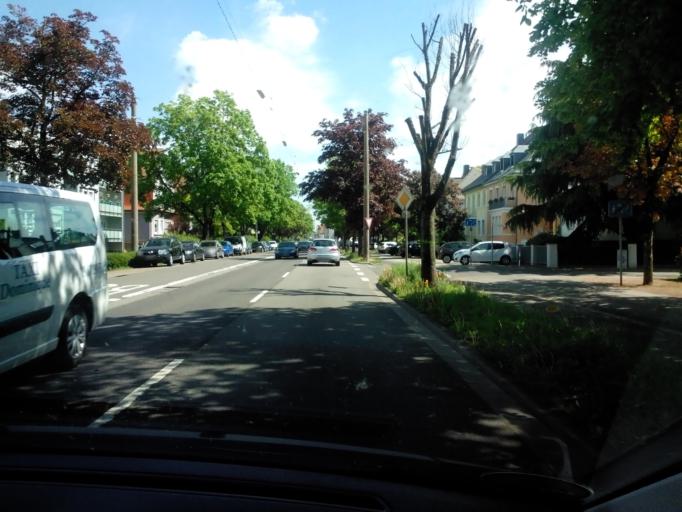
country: DE
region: Saarland
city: Saarlouis
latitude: 49.3085
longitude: 6.7452
